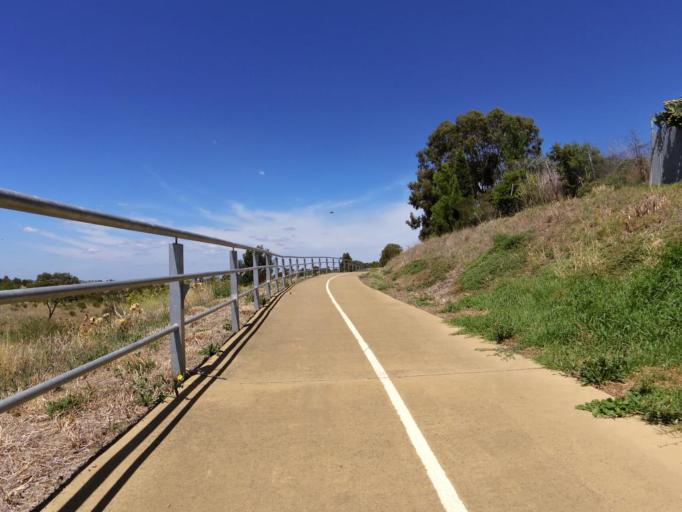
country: AU
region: Victoria
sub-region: Hume
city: Campbellfield
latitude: -37.6697
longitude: 144.9731
